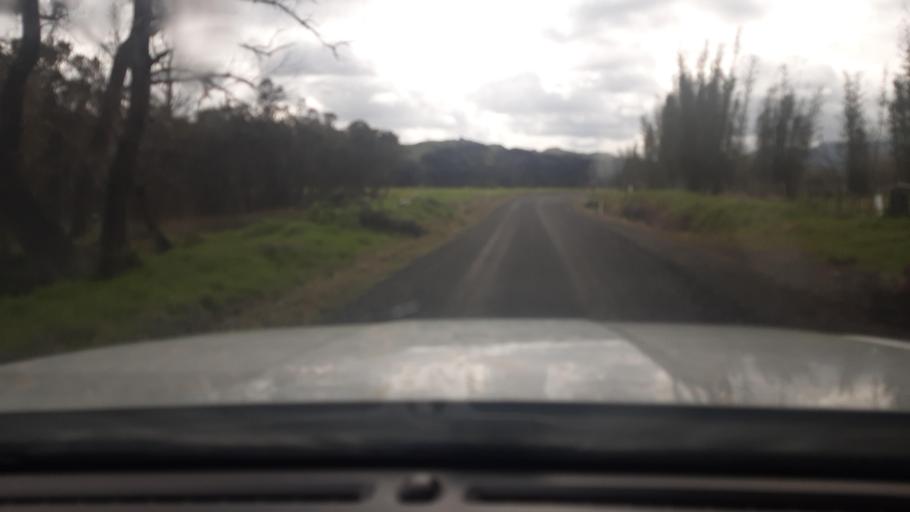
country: NZ
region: Northland
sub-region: Far North District
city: Ahipara
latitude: -35.3364
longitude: 173.2216
